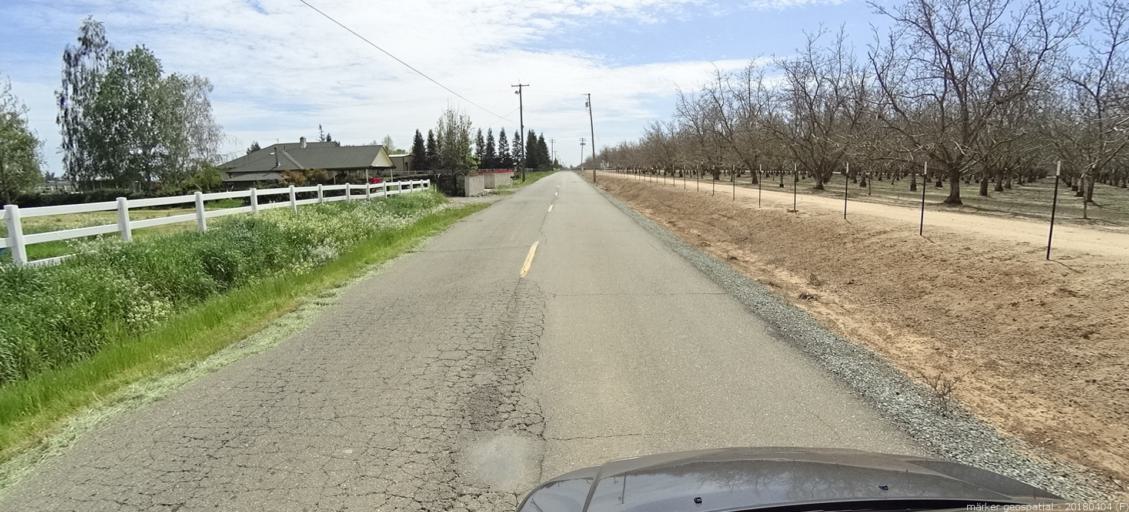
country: US
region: California
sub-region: Sacramento County
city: Herald
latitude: 38.3040
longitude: -121.2080
